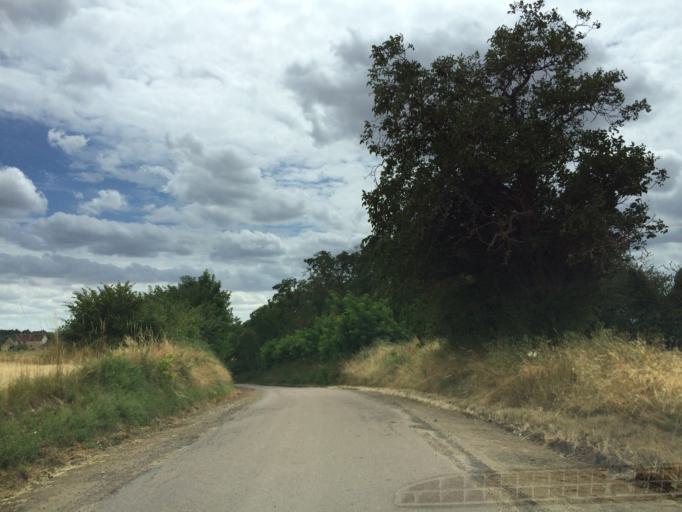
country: FR
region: Bourgogne
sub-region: Departement de l'Yonne
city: Fleury-la-Vallee
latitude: 47.8502
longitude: 3.4045
